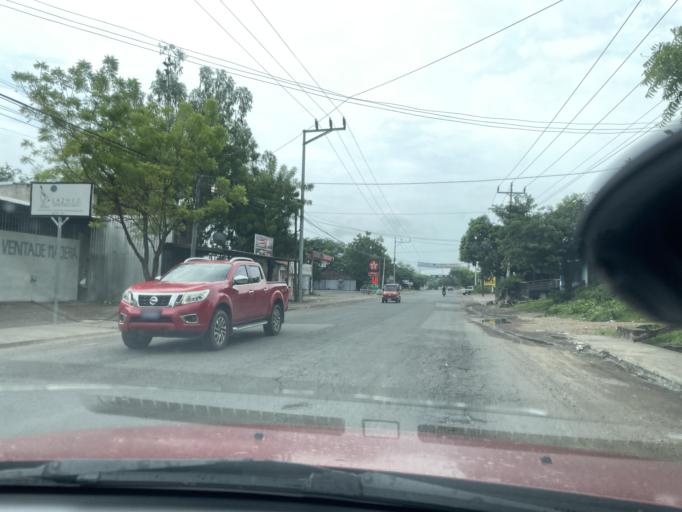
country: SV
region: La Union
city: Santa Rosa de Lima
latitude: 13.6298
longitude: -87.8858
